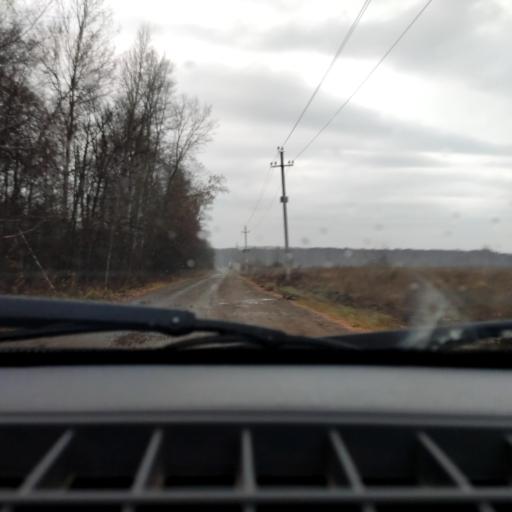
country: RU
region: Bashkortostan
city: Avdon
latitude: 54.6298
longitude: 55.7347
